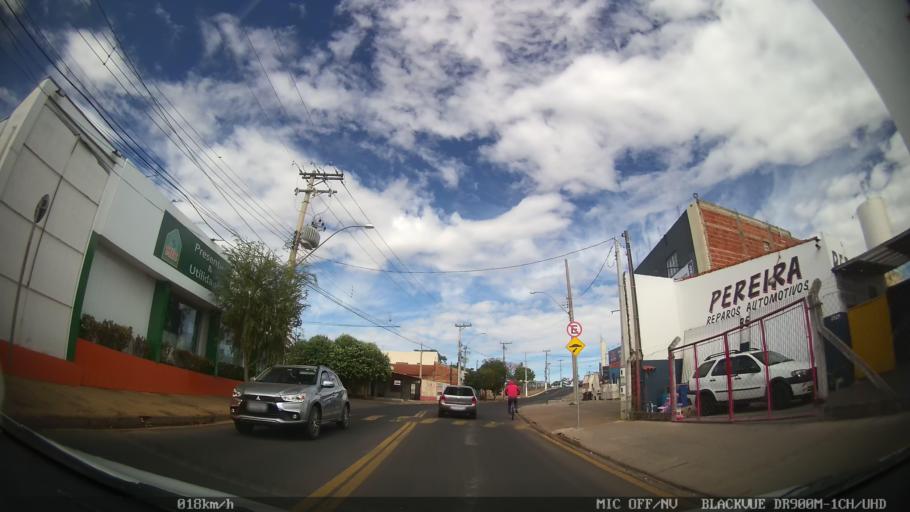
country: BR
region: Sao Paulo
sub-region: Sao Jose Do Rio Preto
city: Sao Jose do Rio Preto
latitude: -20.8061
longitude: -49.5057
